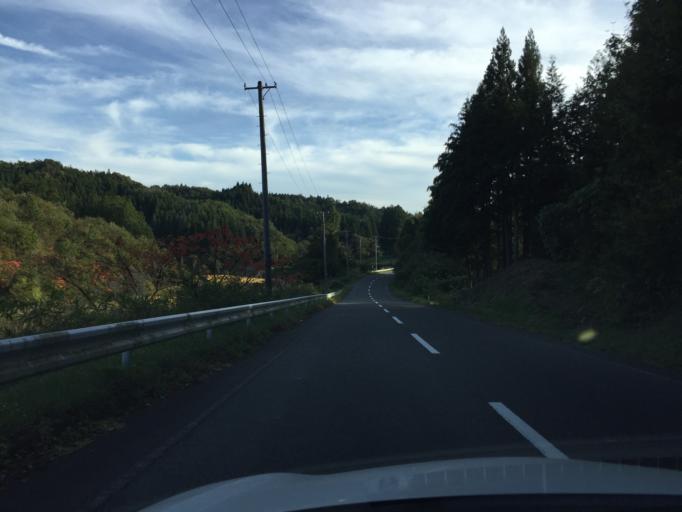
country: JP
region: Fukushima
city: Ishikawa
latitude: 37.2136
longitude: 140.5515
